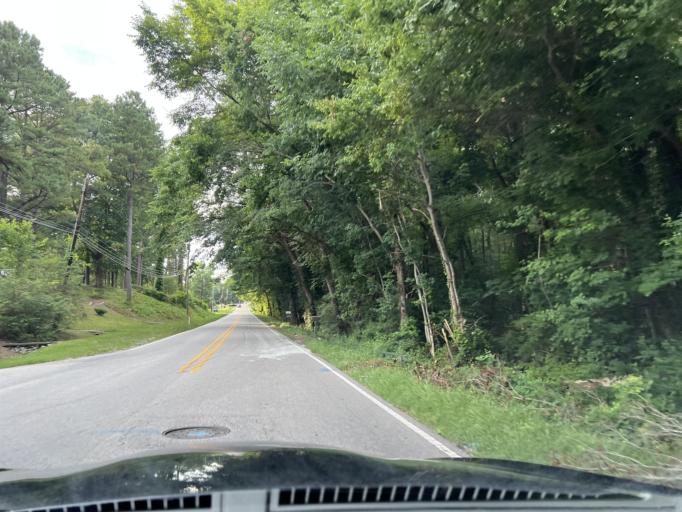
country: US
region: North Carolina
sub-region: Durham County
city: Gorman
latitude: 35.9824
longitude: -78.8420
